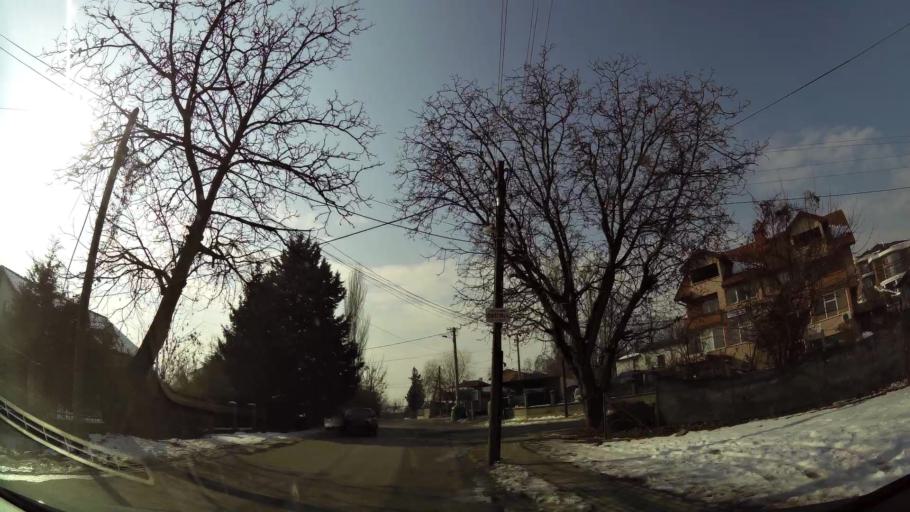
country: MK
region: Suto Orizari
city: Suto Orizare
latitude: 42.0257
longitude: 21.3804
